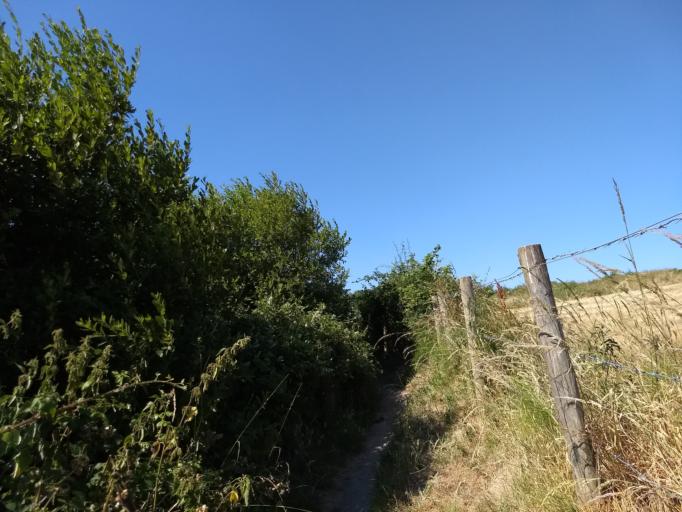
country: GB
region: England
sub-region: Isle of Wight
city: Gurnard
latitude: 50.7459
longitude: -1.3437
